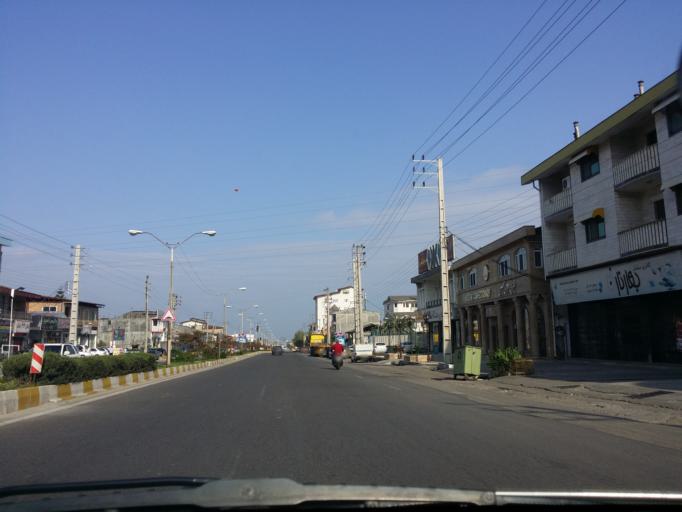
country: IR
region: Mazandaran
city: Chalus
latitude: 36.6704
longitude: 51.4078
